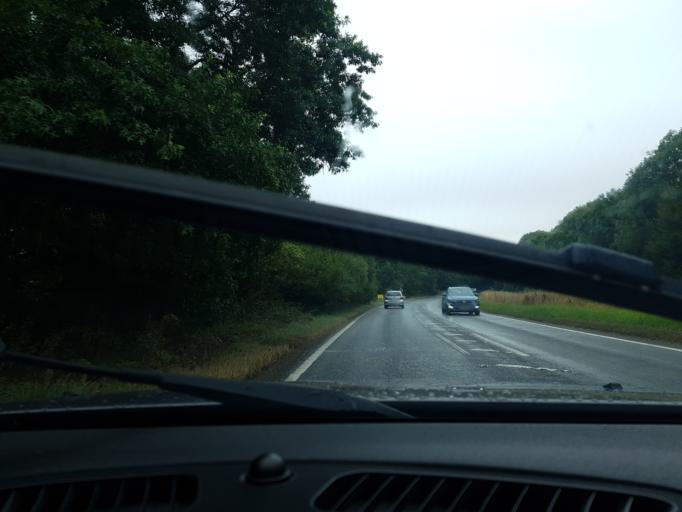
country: GB
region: England
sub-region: Hampshire
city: Odiham
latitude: 51.2468
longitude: -0.8906
